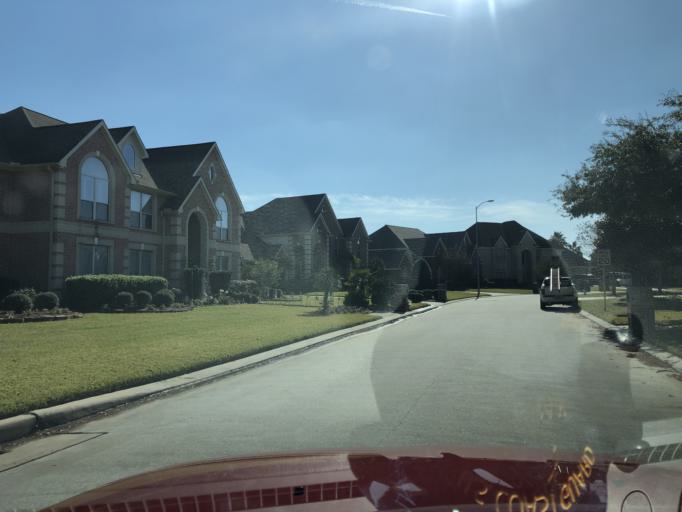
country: US
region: Texas
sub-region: Harris County
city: Tomball
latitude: 30.0368
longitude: -95.5470
